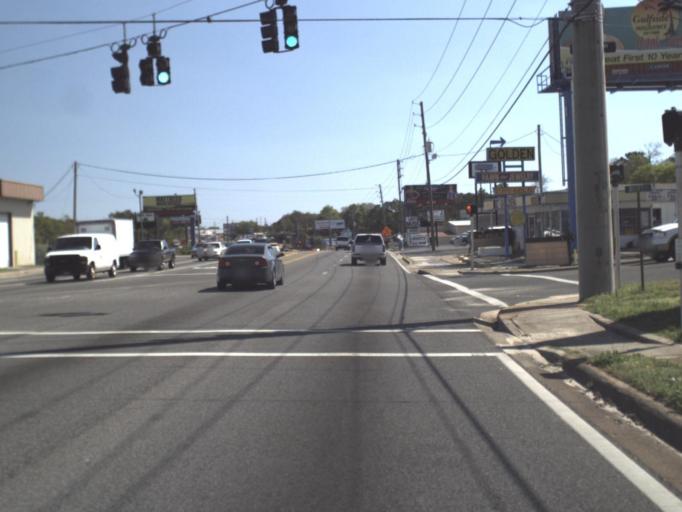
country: US
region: Florida
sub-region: Okaloosa County
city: Wright
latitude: 30.4351
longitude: -86.6392
